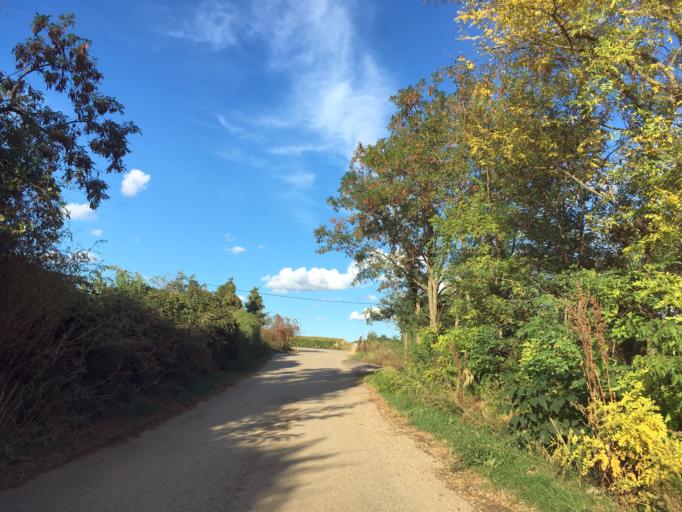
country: SK
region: Nitriansky
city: Svodin
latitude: 47.9160
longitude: 18.4338
